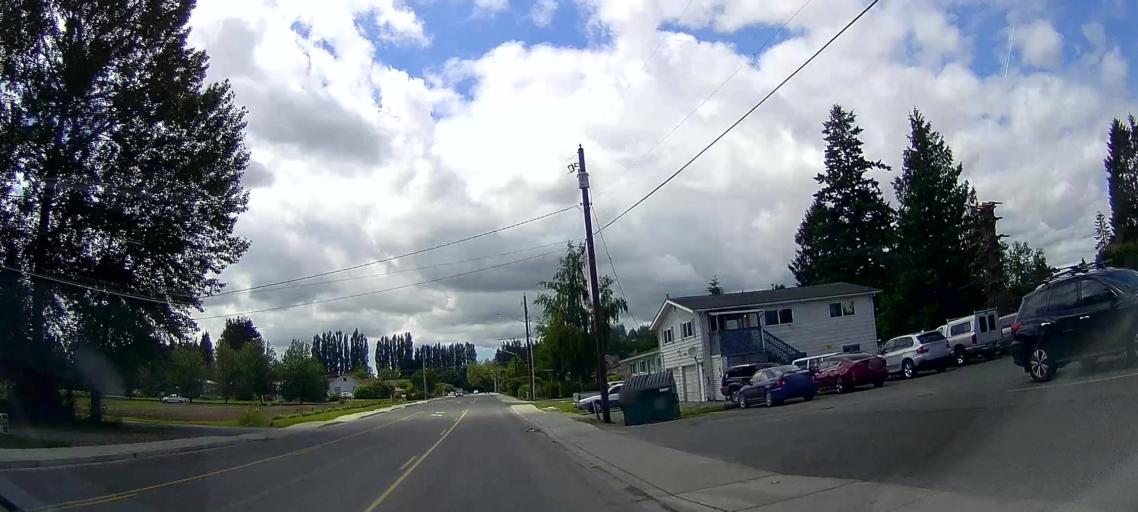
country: US
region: Washington
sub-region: Skagit County
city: Burlington
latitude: 48.4789
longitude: -122.3056
